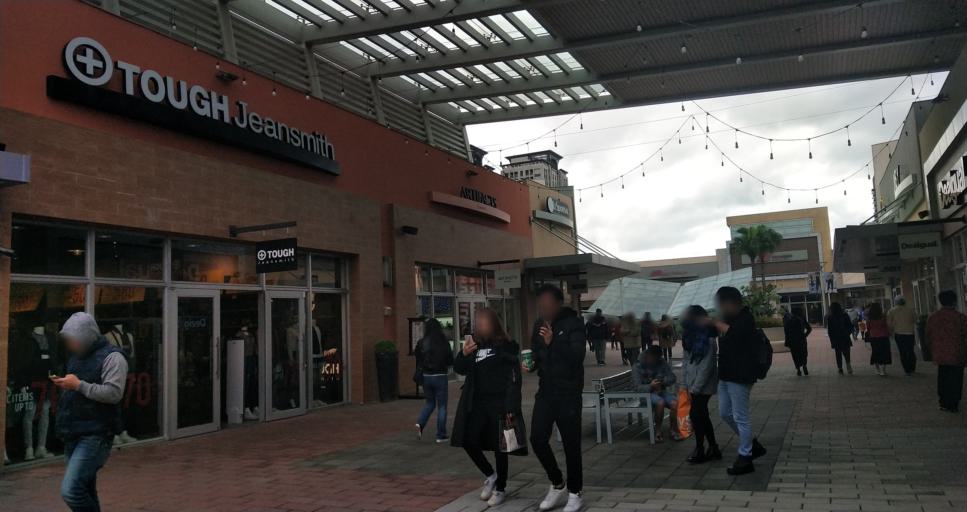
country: TW
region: Taiwan
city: Taoyuan City
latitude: 25.0138
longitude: 121.2124
